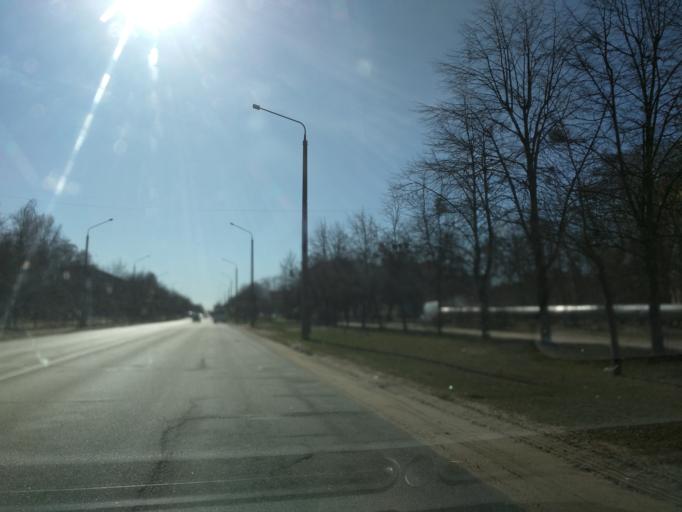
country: BY
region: Mogilev
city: Babruysk
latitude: 53.1768
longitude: 29.1938
